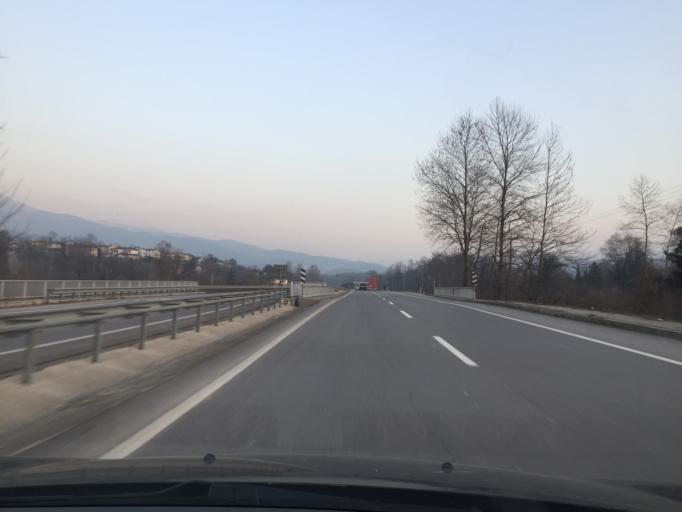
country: TR
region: Sakarya
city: Akyazi
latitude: 40.6331
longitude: 30.6309
